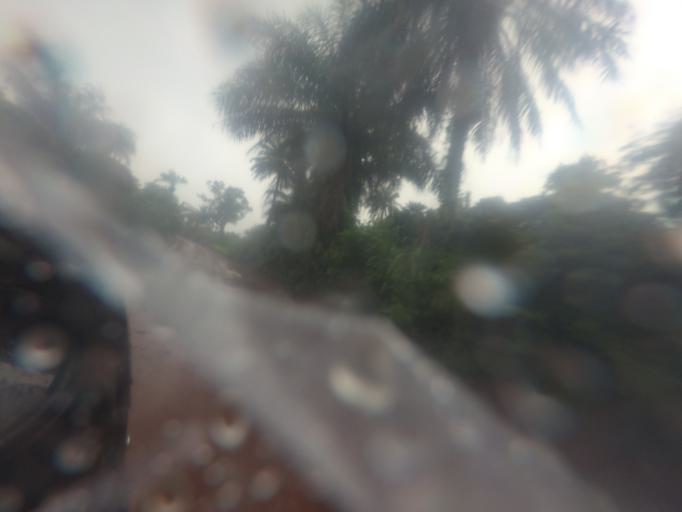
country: SL
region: Northern Province
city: Kambia
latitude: 9.2509
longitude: -12.7863
